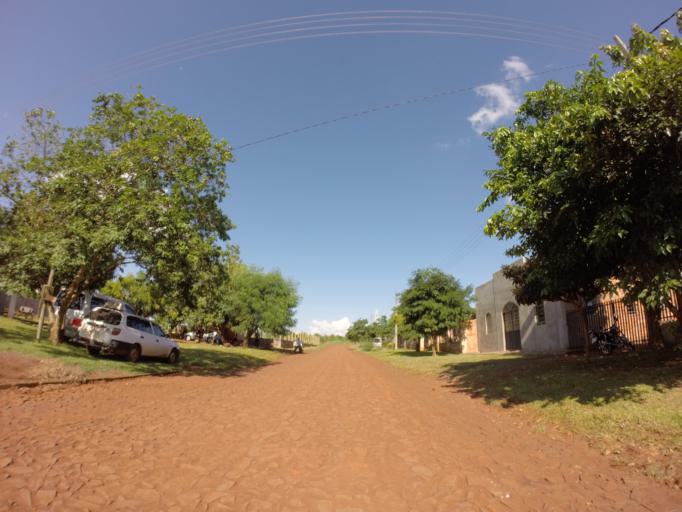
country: PY
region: Alto Parana
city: Ciudad del Este
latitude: -25.3690
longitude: -54.6461
